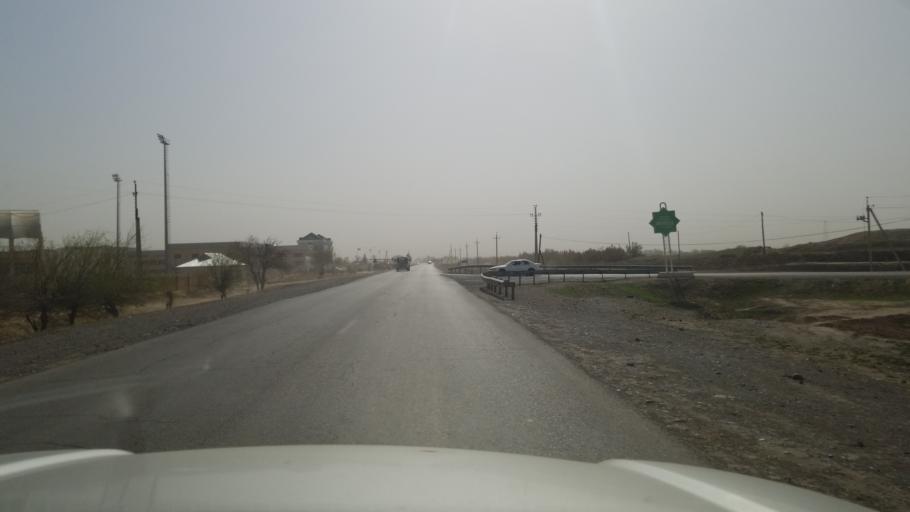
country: TM
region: Mary
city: Yoloeten
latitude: 37.2919
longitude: 62.3393
